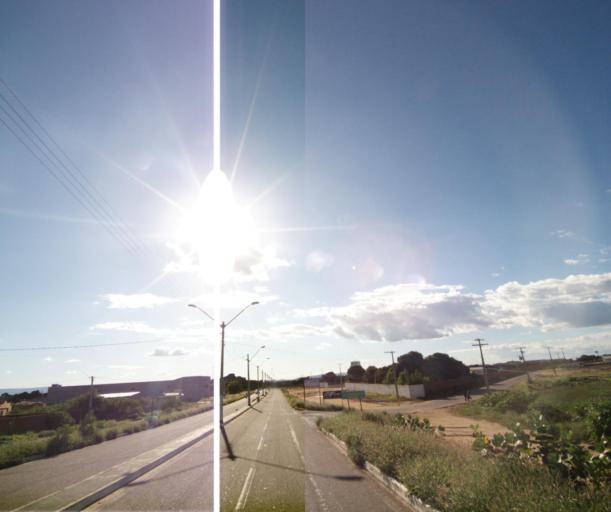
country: BR
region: Bahia
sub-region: Guanambi
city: Guanambi
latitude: -14.2110
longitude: -42.7950
